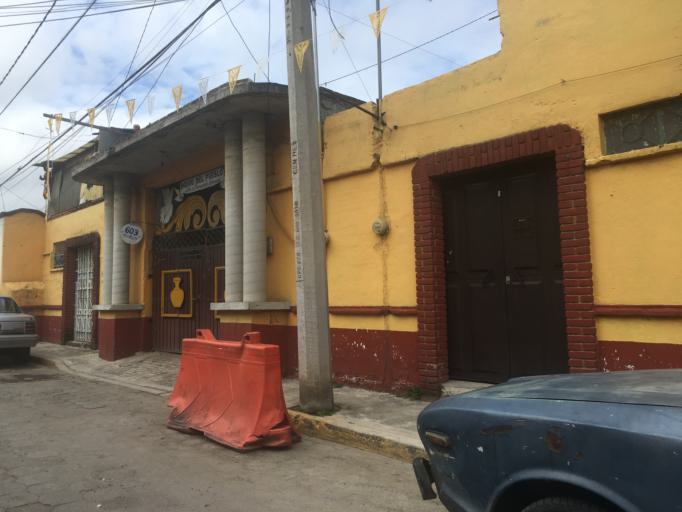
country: MX
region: Morelos
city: Metepec
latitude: 19.2601
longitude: -99.6079
